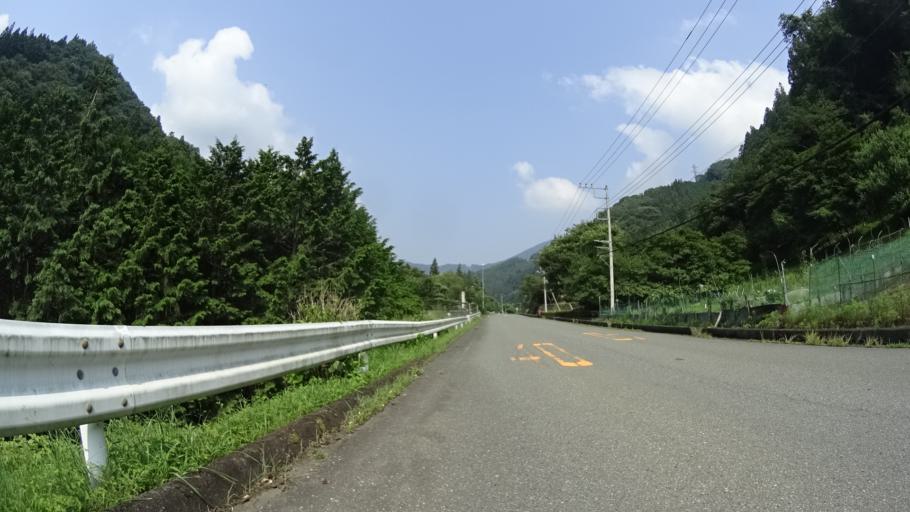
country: JP
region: Gunma
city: Tomioka
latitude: 36.0518
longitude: 138.8726
